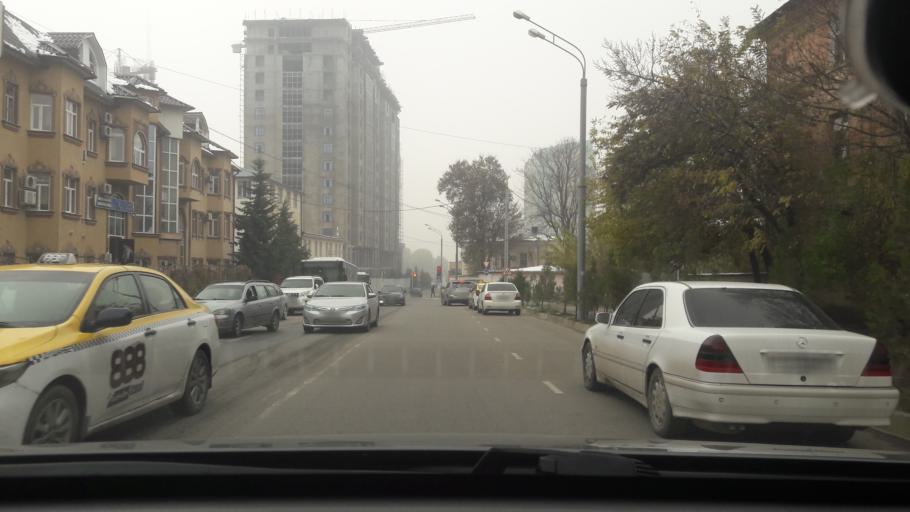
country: TJ
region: Dushanbe
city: Dushanbe
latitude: 38.5768
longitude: 68.8002
